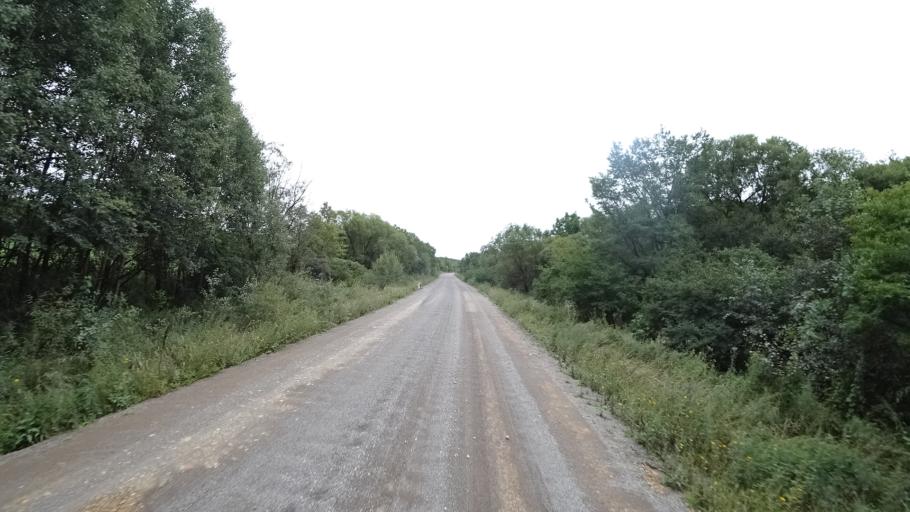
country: RU
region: Primorskiy
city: Ivanovka
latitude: 44.0534
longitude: 132.4831
